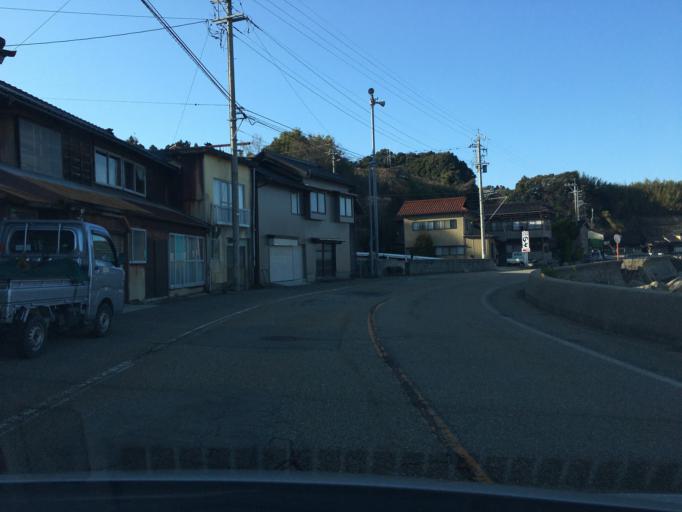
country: JP
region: Ishikawa
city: Nanao
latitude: 36.9604
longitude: 137.0513
